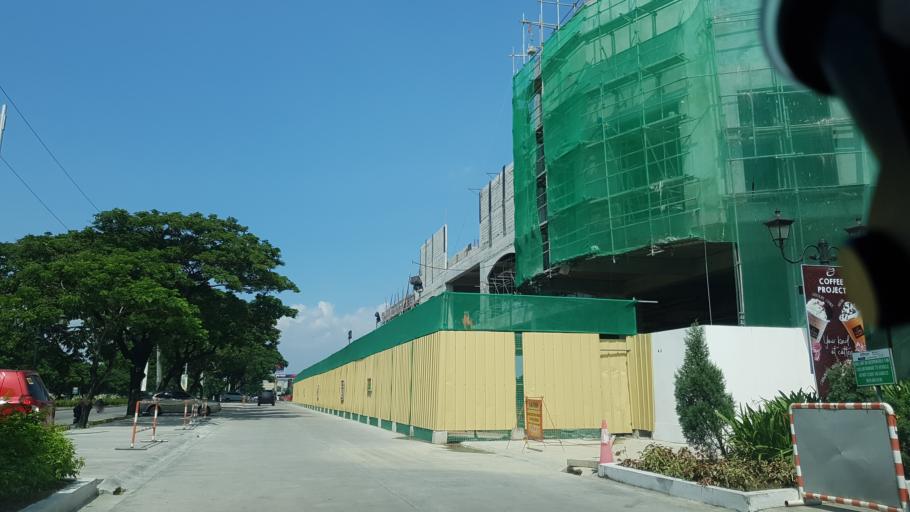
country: PH
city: Sambayanihan People's Village
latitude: 14.4773
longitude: 120.9844
